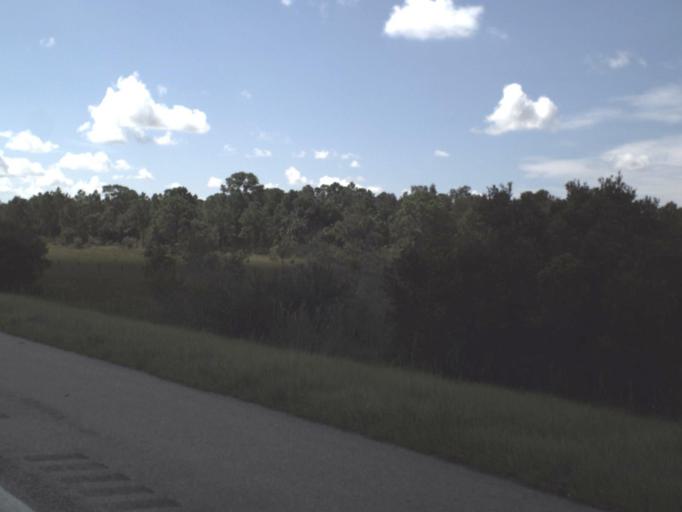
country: US
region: Florida
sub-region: Lee County
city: Suncoast Estates
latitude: 26.7832
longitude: -81.8992
